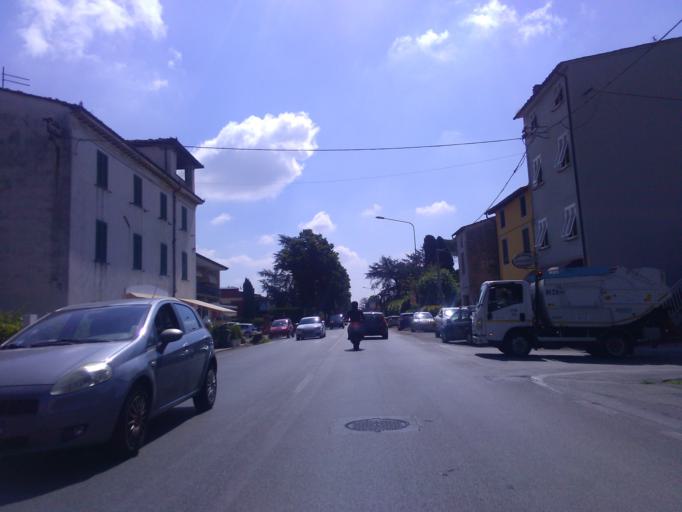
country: IT
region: Tuscany
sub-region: Provincia di Lucca
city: Lucca
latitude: 43.8493
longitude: 10.4635
